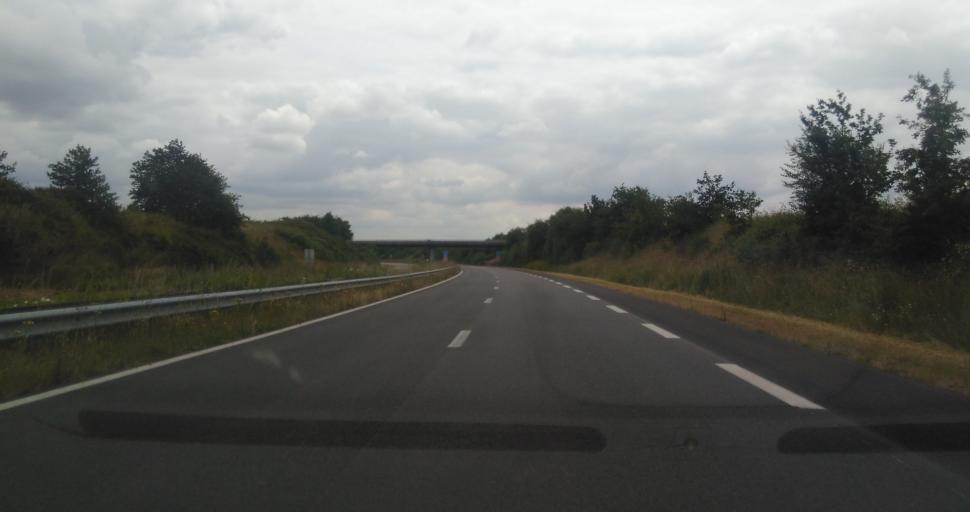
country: FR
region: Pays de la Loire
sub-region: Departement de la Vendee
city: Bournezeau
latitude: 46.6324
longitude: -1.1791
